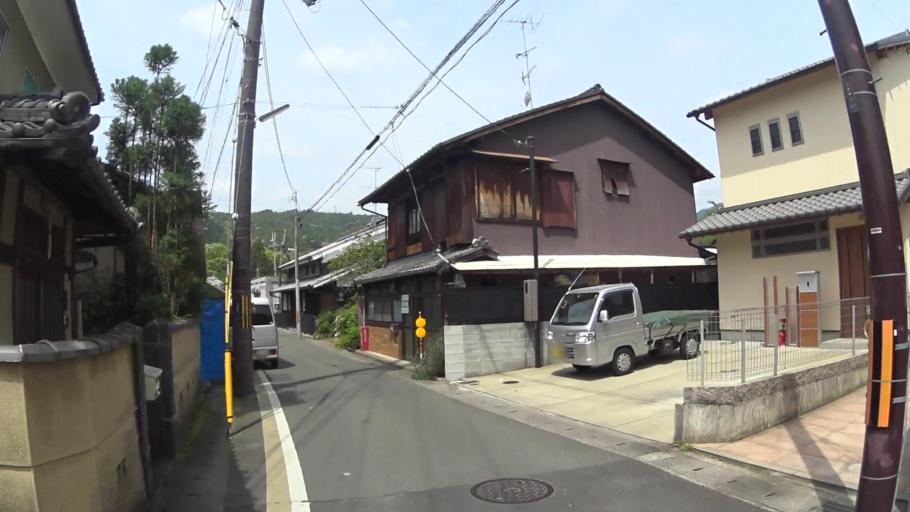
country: JP
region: Kyoto
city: Muko
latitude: 35.0232
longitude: 135.6771
